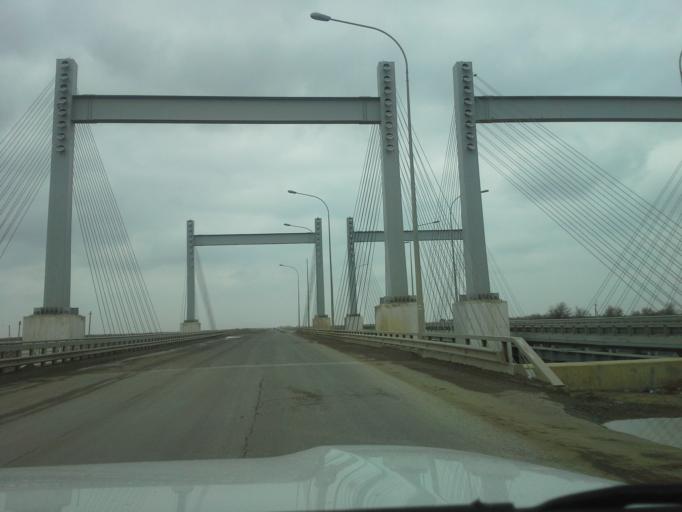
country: TM
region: Ahal
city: Tejen
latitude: 37.2339
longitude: 60.8593
